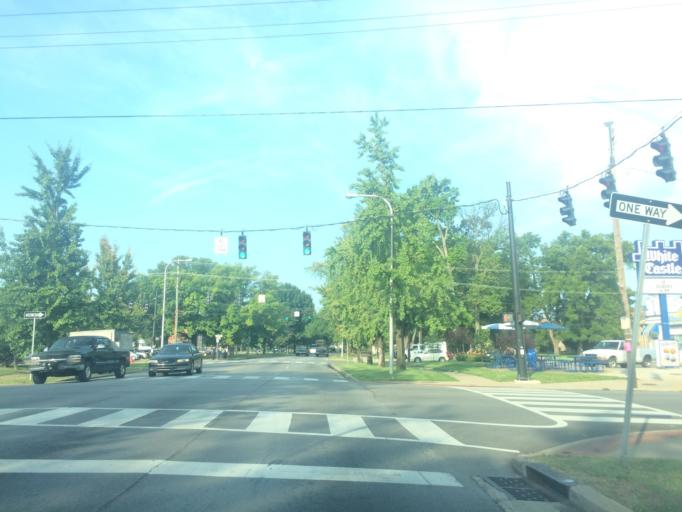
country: US
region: Kentucky
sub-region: Jefferson County
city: Audubon Park
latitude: 38.2150
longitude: -85.7425
